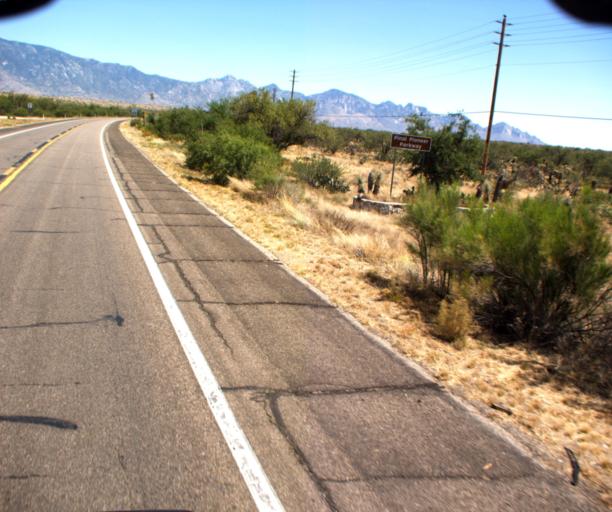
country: US
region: Arizona
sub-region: Pima County
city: Catalina
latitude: 32.5615
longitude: -110.9376
